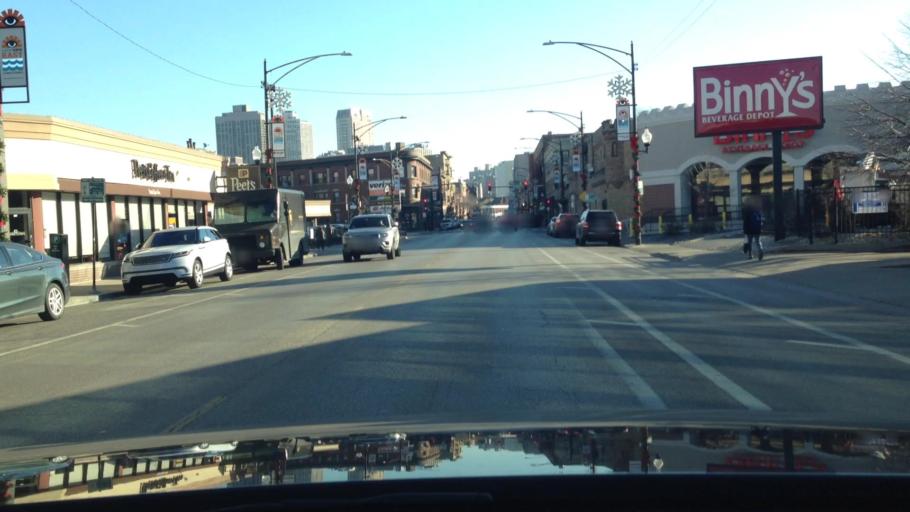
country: US
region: Illinois
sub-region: Cook County
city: Chicago
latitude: 41.9374
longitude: -87.6487
